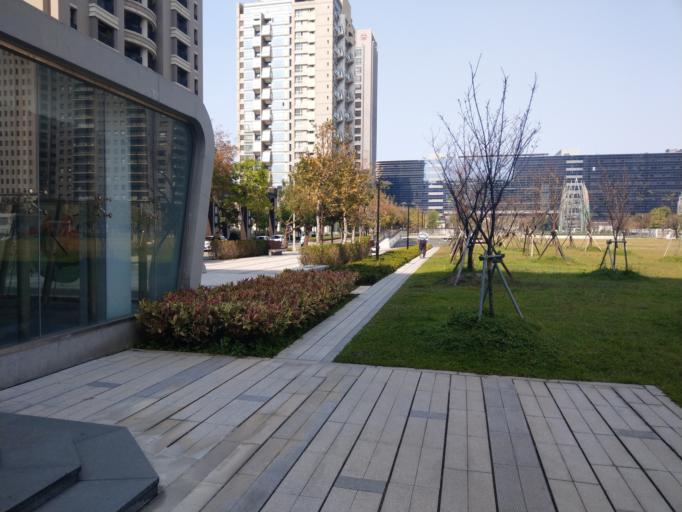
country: TW
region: Taiwan
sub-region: Taichung City
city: Taichung
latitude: 24.1592
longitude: 120.6448
